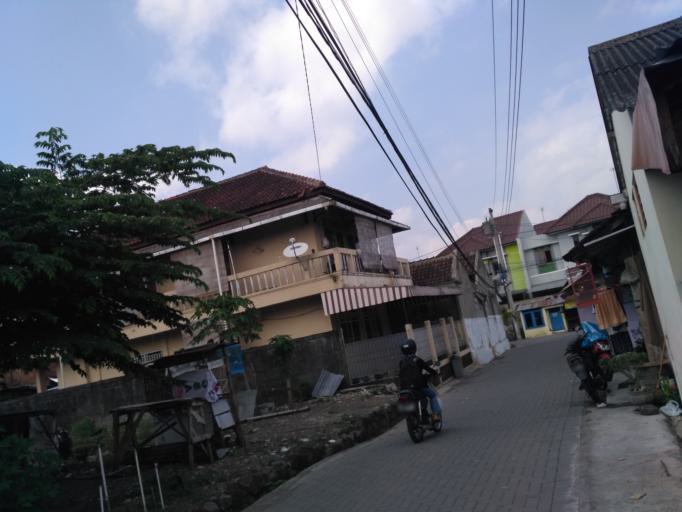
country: ID
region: Daerah Istimewa Yogyakarta
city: Melati
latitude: -7.7549
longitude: 110.3751
